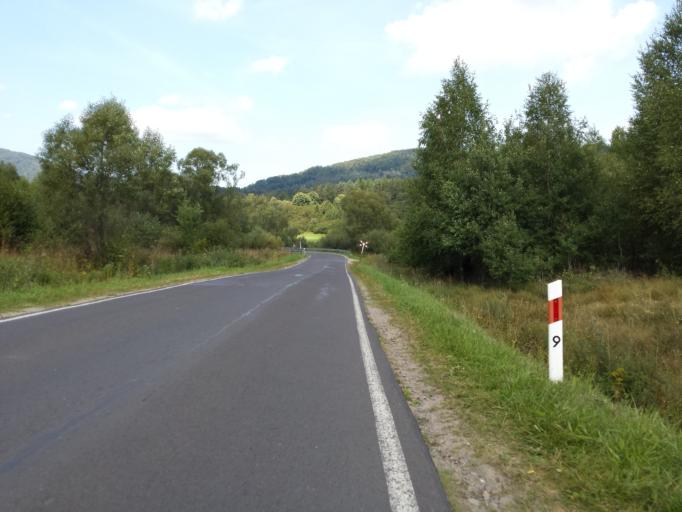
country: PL
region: Subcarpathian Voivodeship
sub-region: Powiat leski
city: Cisna
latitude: 49.1798
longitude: 22.4347
